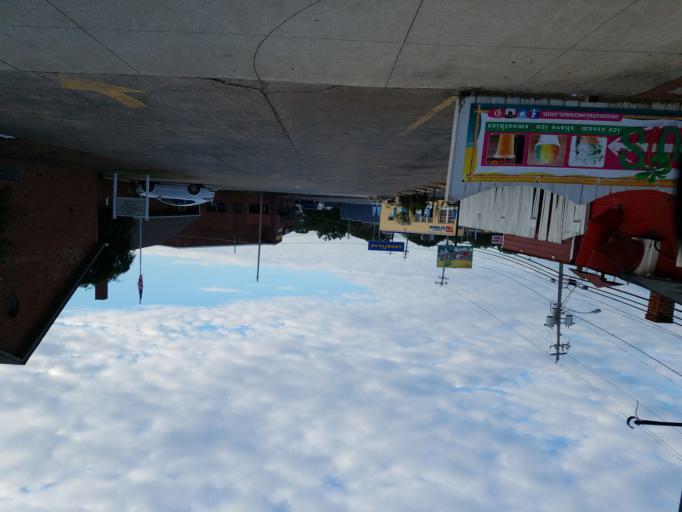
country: US
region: Georgia
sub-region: Bartow County
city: Cartersville
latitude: 34.1654
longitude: -84.7945
